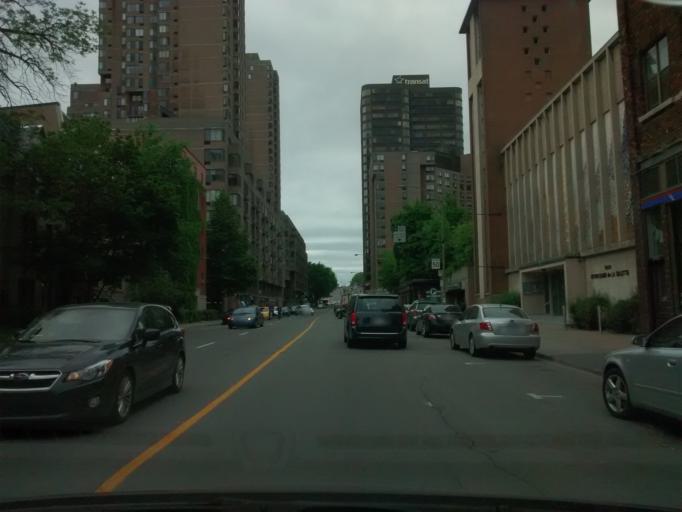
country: CA
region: Quebec
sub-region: Montreal
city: Montreal
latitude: 45.5097
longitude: -73.5739
